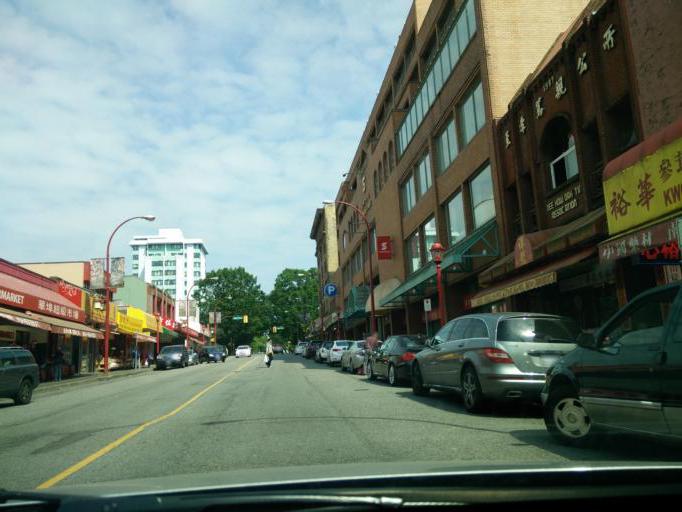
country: CA
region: British Columbia
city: West End
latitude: 49.2795
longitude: -123.0987
